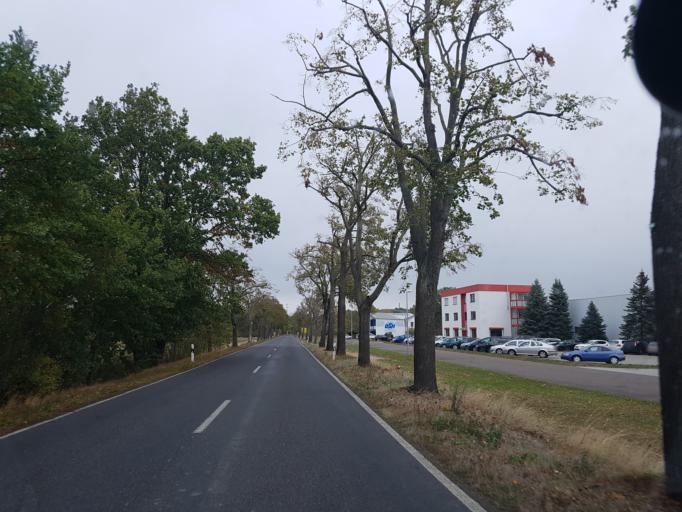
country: DE
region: Brandenburg
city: Falkenberg
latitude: 51.6007
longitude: 13.2367
